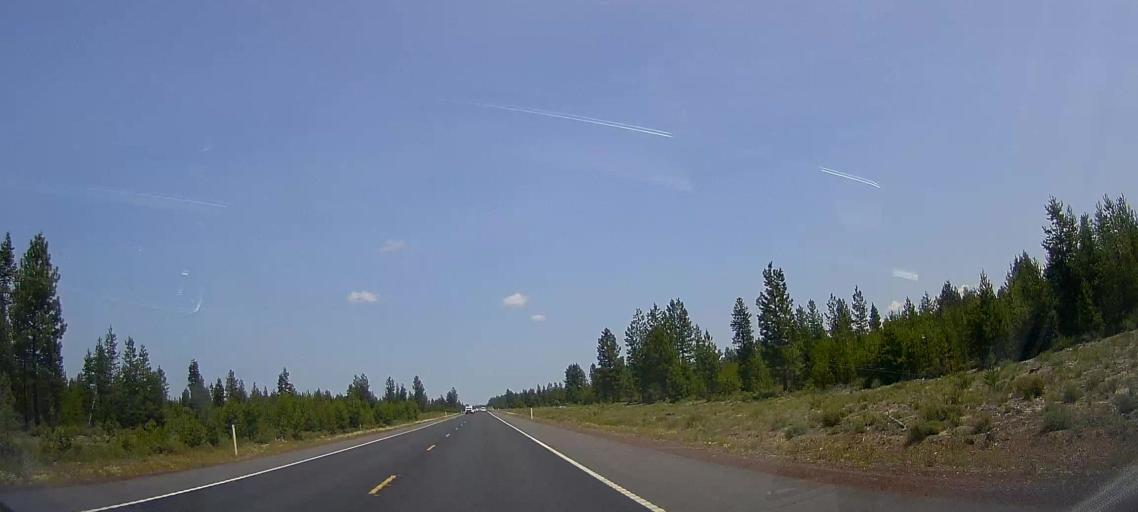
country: US
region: Oregon
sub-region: Deschutes County
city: La Pine
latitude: 43.4986
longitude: -121.6706
